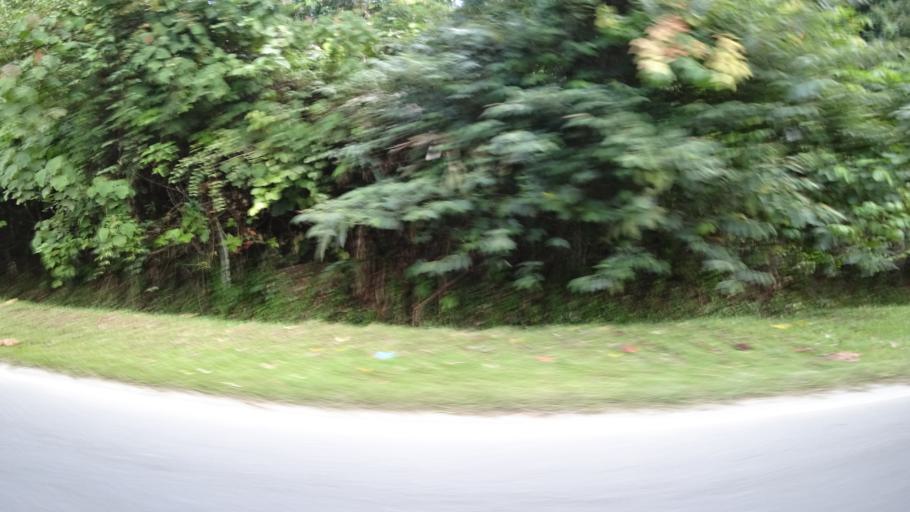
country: MY
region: Sarawak
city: Limbang
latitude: 4.7207
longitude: 114.9912
